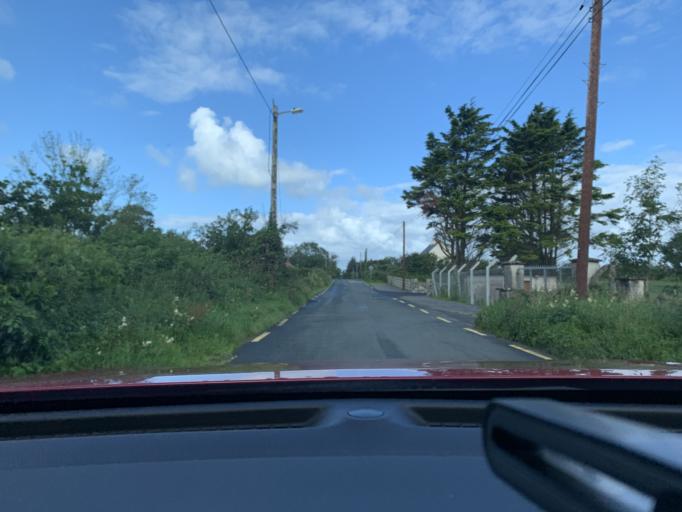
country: IE
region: Connaught
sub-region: Sligo
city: Strandhill
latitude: 54.3927
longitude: -8.5321
